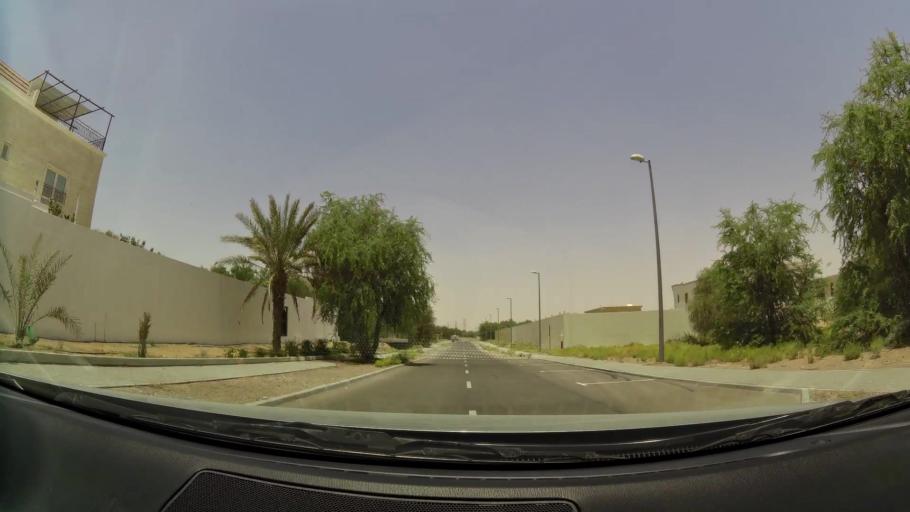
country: OM
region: Al Buraimi
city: Al Buraymi
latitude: 24.2819
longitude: 55.7369
